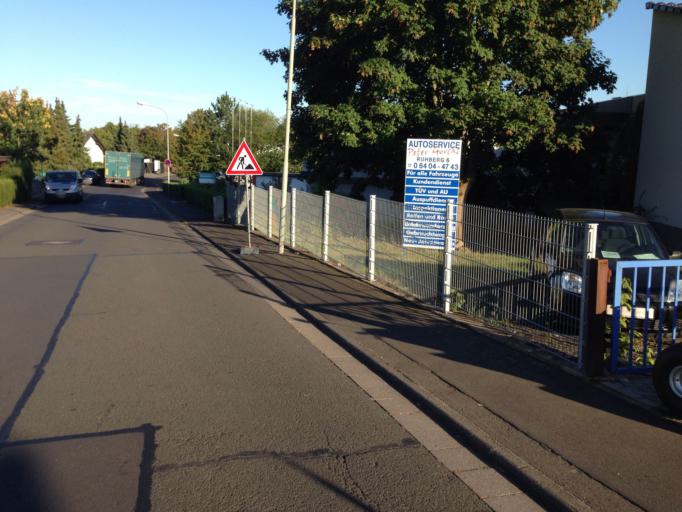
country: DE
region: Hesse
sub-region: Regierungsbezirk Giessen
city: Lich
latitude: 50.5477
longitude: 8.7728
